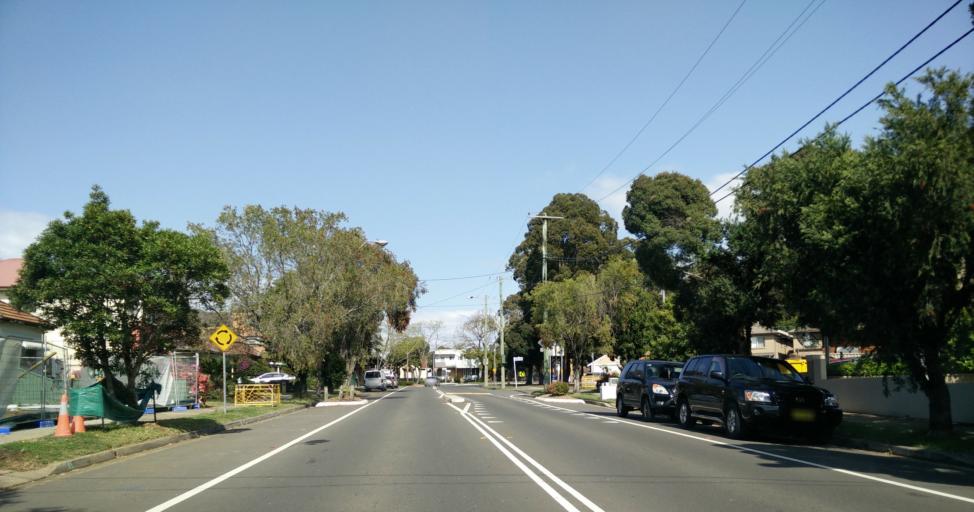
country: AU
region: New South Wales
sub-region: Bankstown
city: Padstow
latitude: -33.9481
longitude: 151.0305
